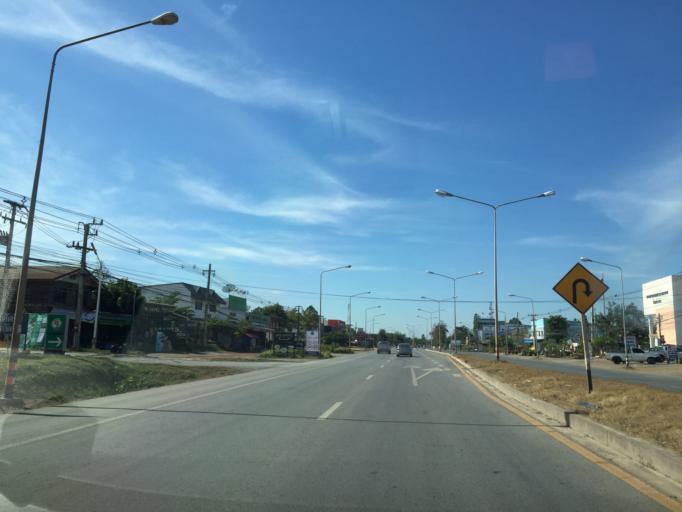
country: TH
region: Changwat Nong Bua Lamphu
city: Na Klang
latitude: 17.3035
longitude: 102.1978
